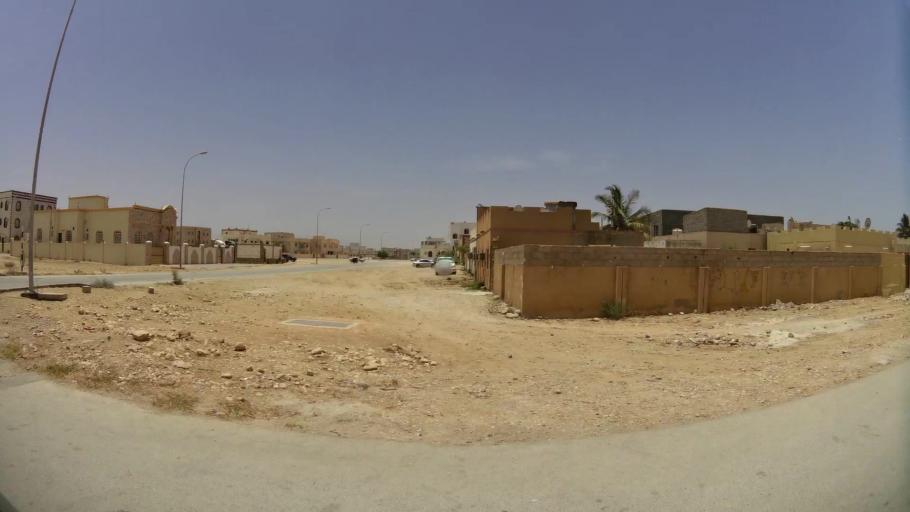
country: OM
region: Zufar
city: Salalah
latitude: 17.0826
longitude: 54.1517
